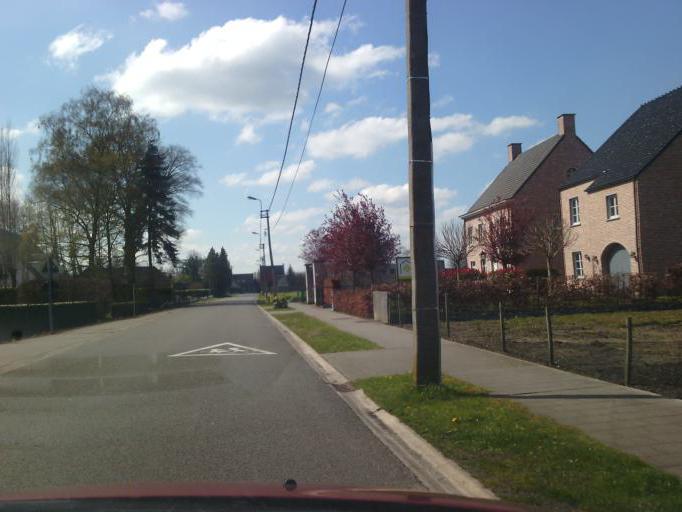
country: BE
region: Flanders
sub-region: Provincie Oost-Vlaanderen
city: Wichelen
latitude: 51.0492
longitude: 3.9509
